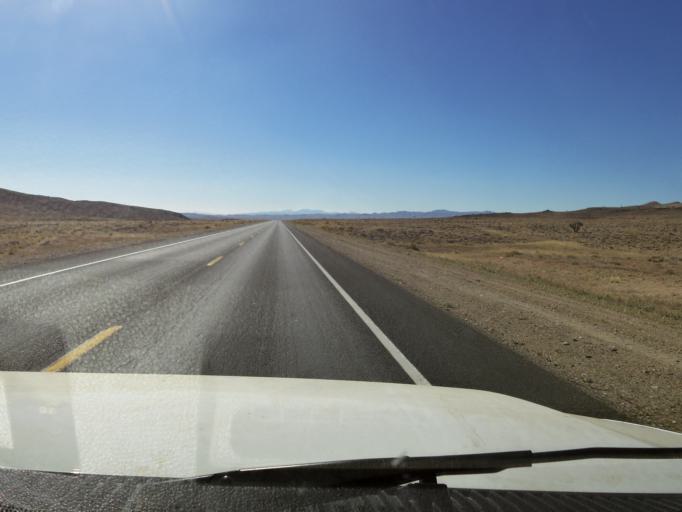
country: US
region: Nevada
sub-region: Esmeralda County
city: Goldfield
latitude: 37.5533
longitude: -117.1974
